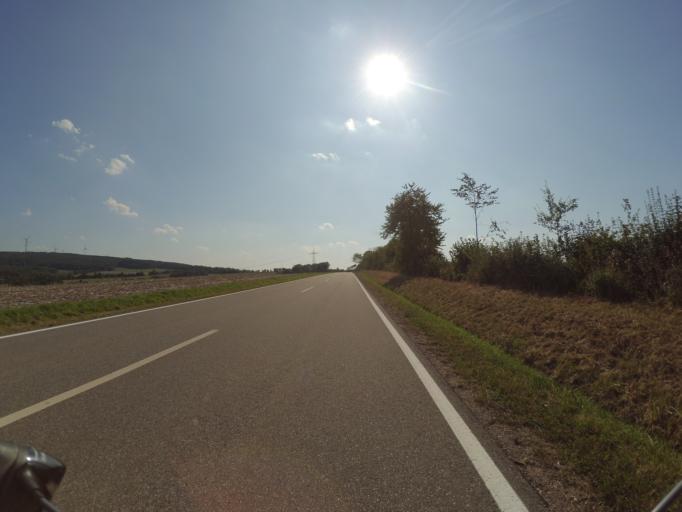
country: DE
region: Rheinland-Pfalz
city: Wintrich
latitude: 49.8791
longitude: 6.9671
